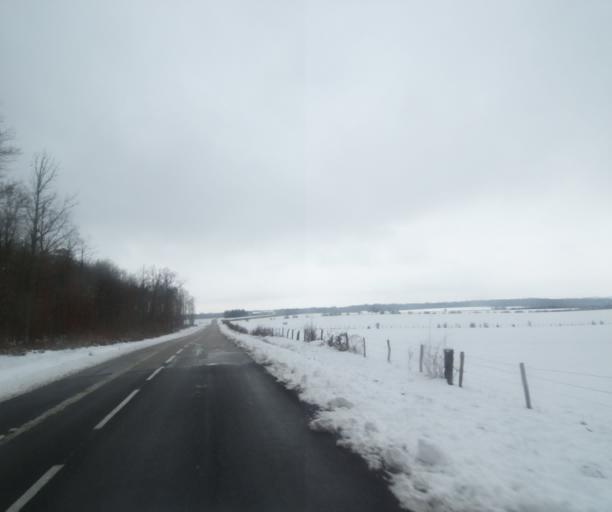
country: FR
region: Champagne-Ardenne
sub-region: Departement de la Haute-Marne
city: Laneuville-a-Remy
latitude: 48.4399
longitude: 4.8579
